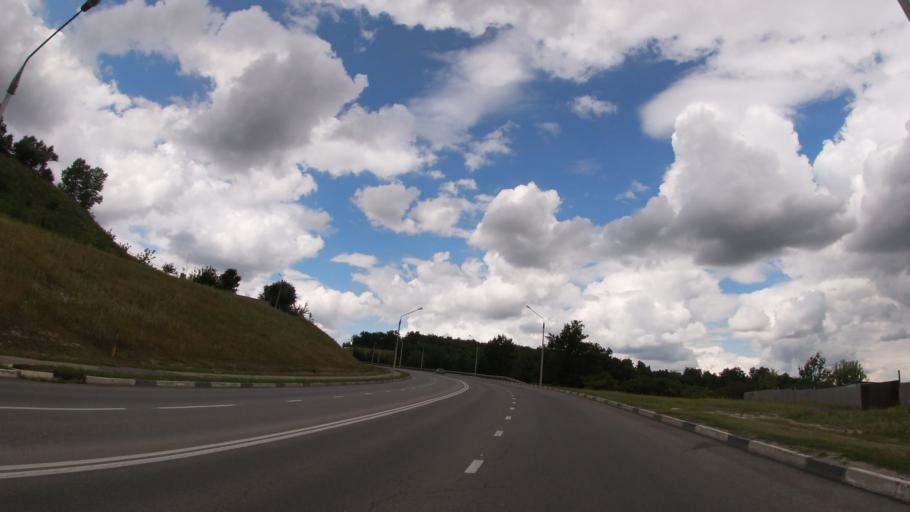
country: RU
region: Belgorod
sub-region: Belgorodskiy Rayon
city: Belgorod
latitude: 50.6198
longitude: 36.6164
